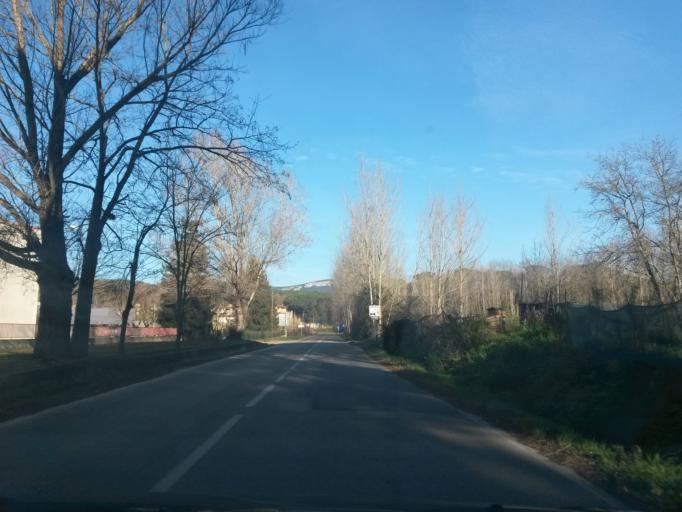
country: ES
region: Catalonia
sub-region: Provincia de Girona
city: Angles
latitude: 41.9705
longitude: 2.6706
